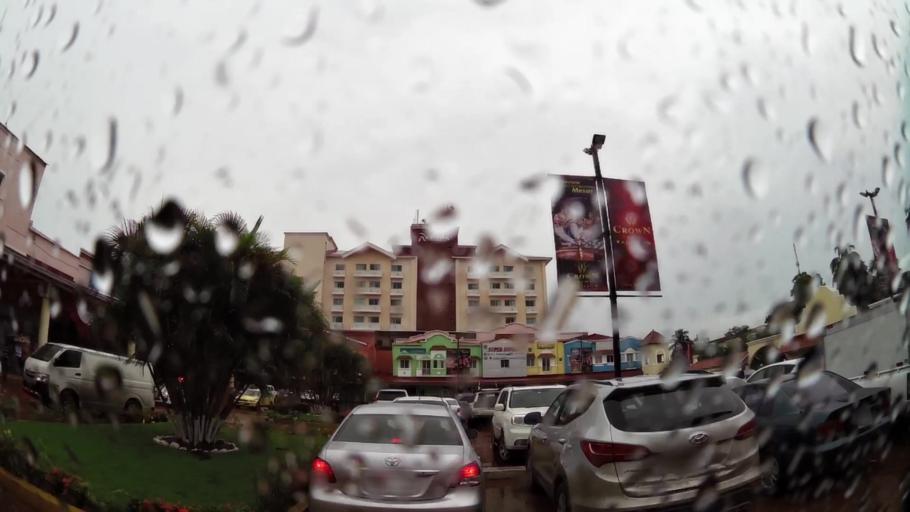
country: PA
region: Colon
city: Colon
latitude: 9.3574
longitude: -79.8923
